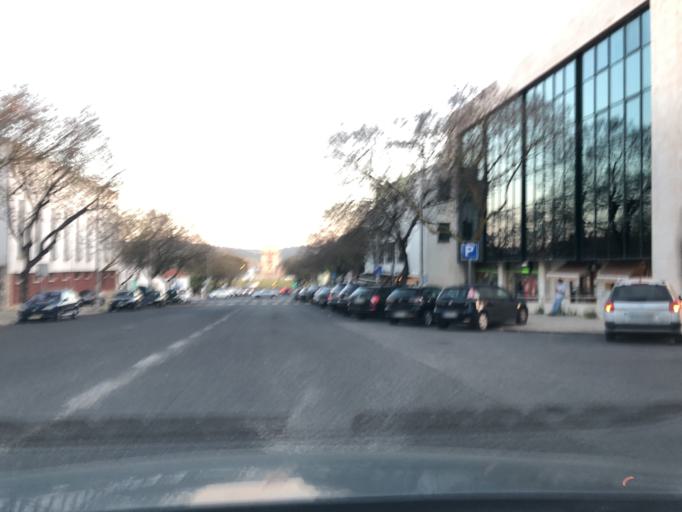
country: PT
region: Lisbon
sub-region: Oeiras
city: Alges
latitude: 38.6959
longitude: -9.2149
